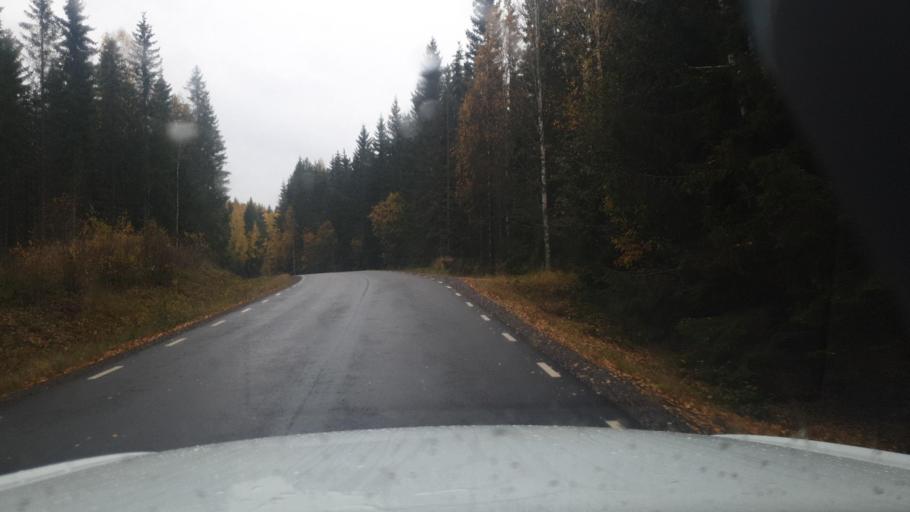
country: SE
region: Vaermland
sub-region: Torsby Kommun
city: Torsby
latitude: 60.0001
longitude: 12.7335
